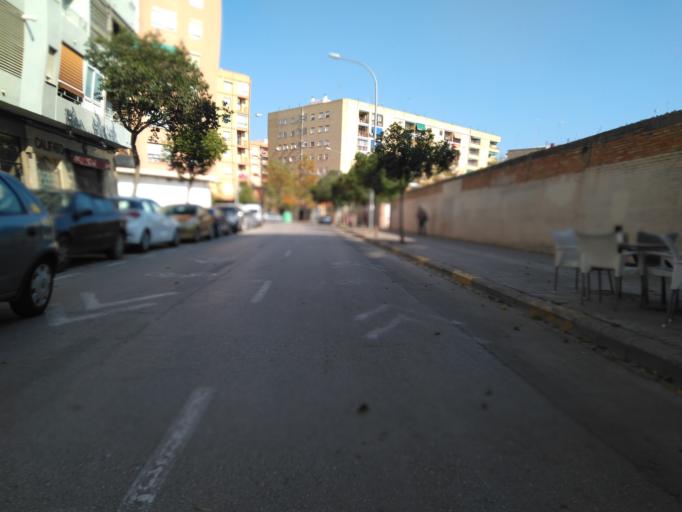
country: ES
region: Valencia
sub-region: Provincia de Valencia
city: Tavernes Blanques
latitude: 39.4918
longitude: -0.3868
